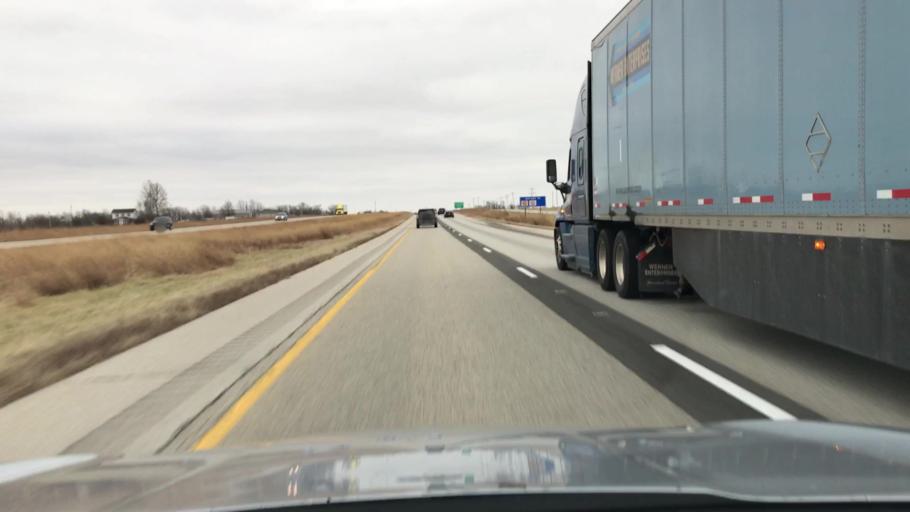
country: US
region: Illinois
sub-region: Sangamon County
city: Divernon
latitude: 39.4686
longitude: -89.6447
